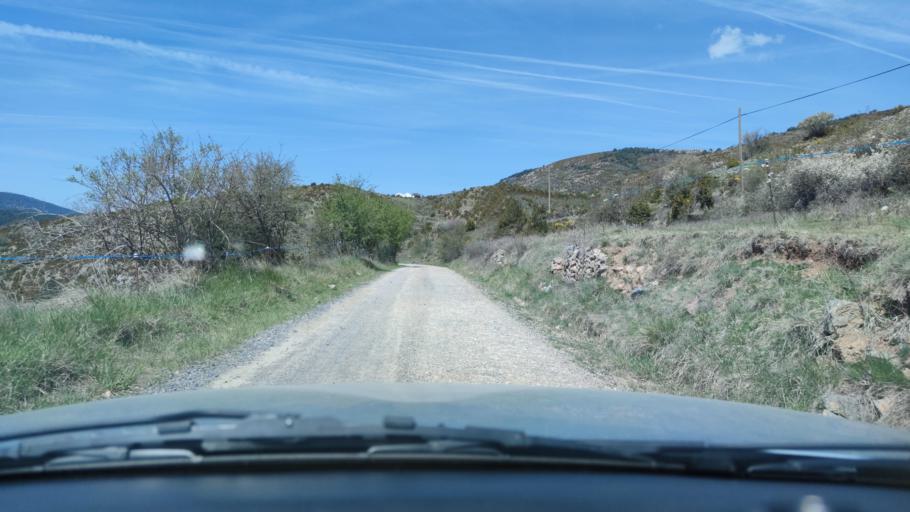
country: ES
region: Catalonia
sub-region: Provincia de Lleida
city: Sort
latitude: 42.2919
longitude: 1.1834
